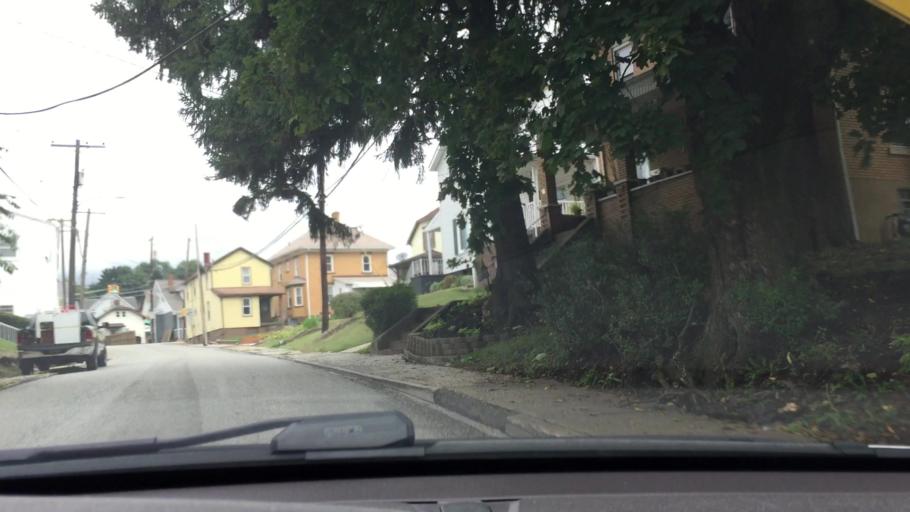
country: US
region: Pennsylvania
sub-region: Washington County
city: Canonsburg
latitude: 40.2571
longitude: -80.1966
